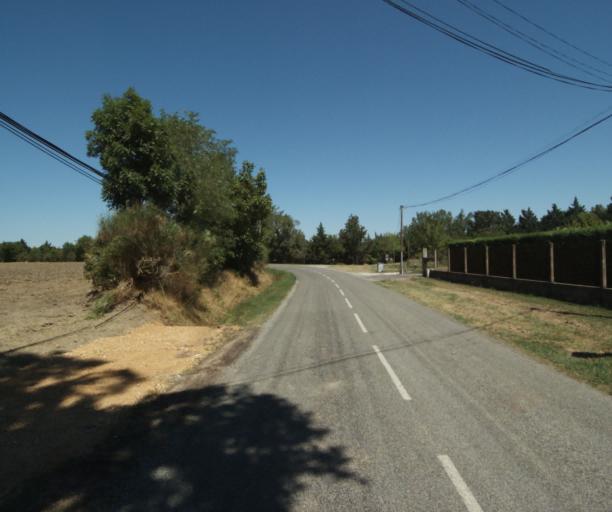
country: FR
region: Midi-Pyrenees
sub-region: Departement de la Haute-Garonne
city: Saint-Felix-Lauragais
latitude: 43.4654
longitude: 1.9297
